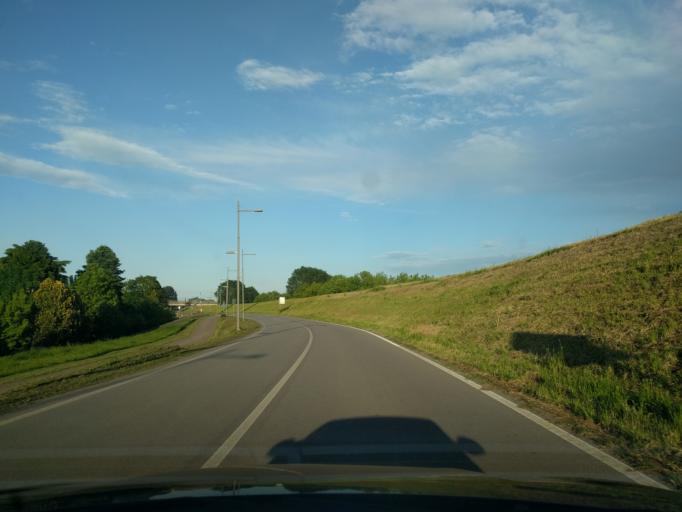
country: IT
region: Veneto
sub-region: Provincia di Rovigo
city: Polesella
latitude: 44.9604
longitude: 11.7501
